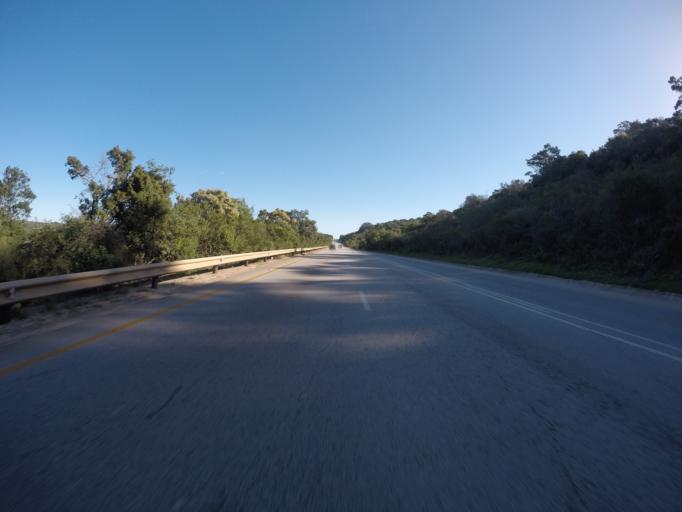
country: ZA
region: Eastern Cape
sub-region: Cacadu District Municipality
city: Jeffrey's Bay
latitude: -33.9039
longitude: 25.0804
